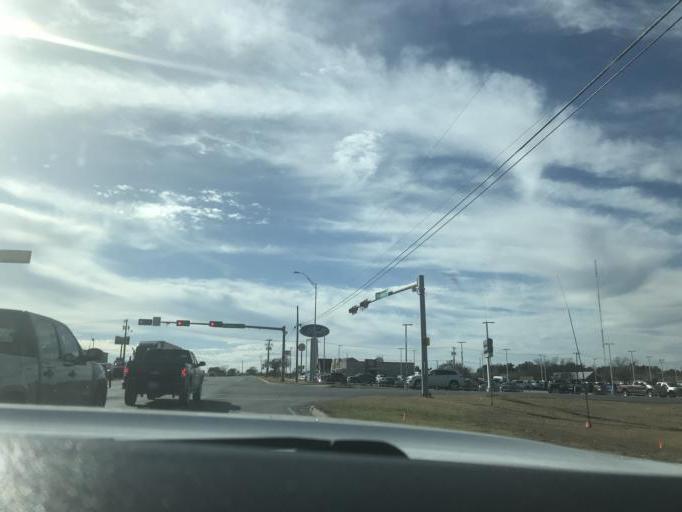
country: US
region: Texas
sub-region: Erath County
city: Stephenville
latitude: 32.2019
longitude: -98.2458
